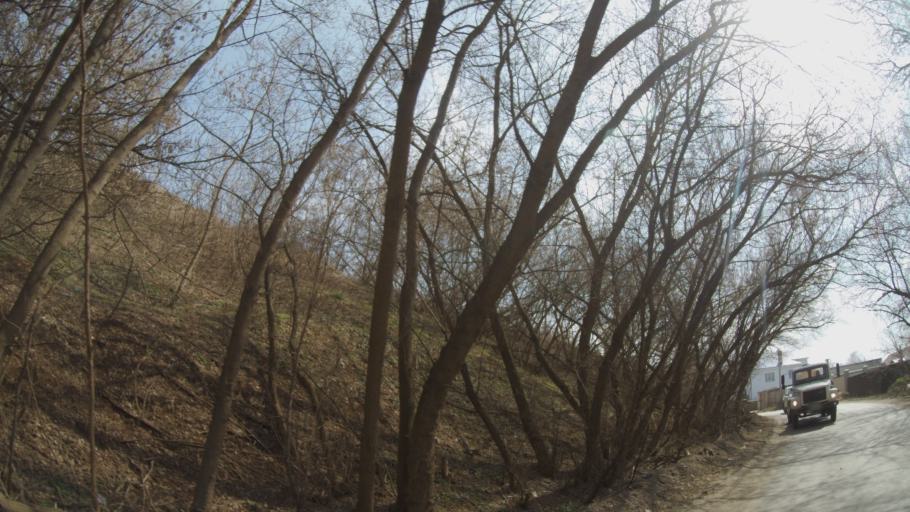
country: RU
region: Nizjnij Novgorod
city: Vyyezdnoye
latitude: 55.3866
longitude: 43.8107
